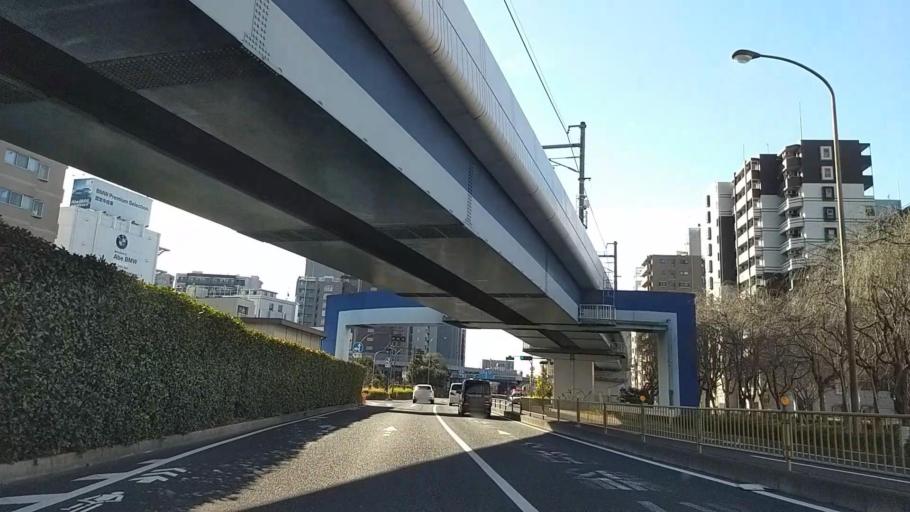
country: JP
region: Kanagawa
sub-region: Kawasaki-shi
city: Kawasaki
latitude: 35.5933
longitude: 139.7364
